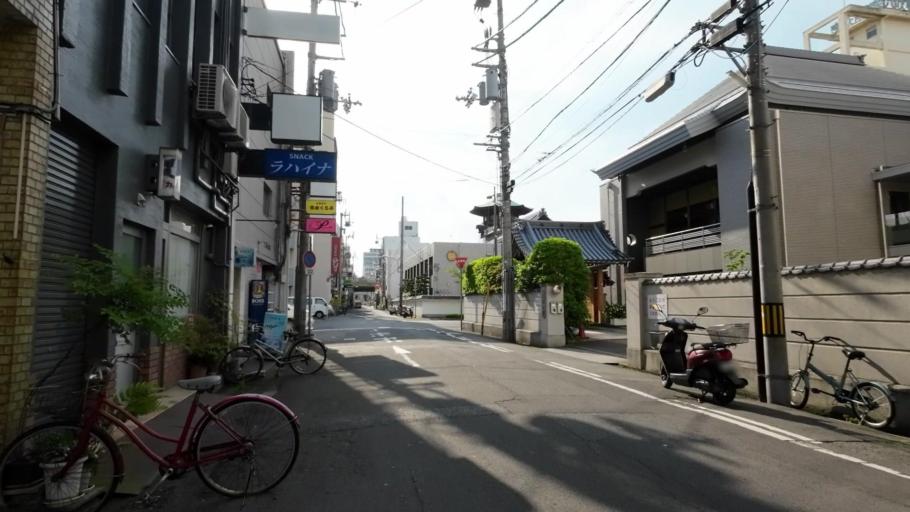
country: JP
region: Kagawa
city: Takamatsu-shi
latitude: 34.3431
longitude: 134.0531
